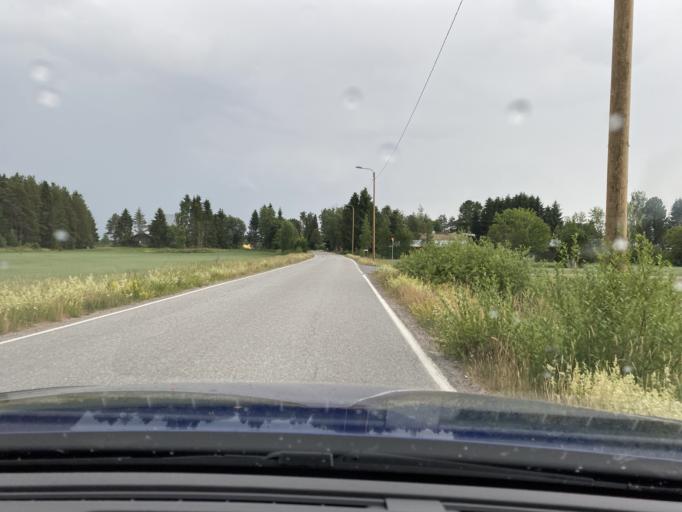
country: FI
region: Satakunta
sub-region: Rauma
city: Eura
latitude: 61.1502
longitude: 22.1218
